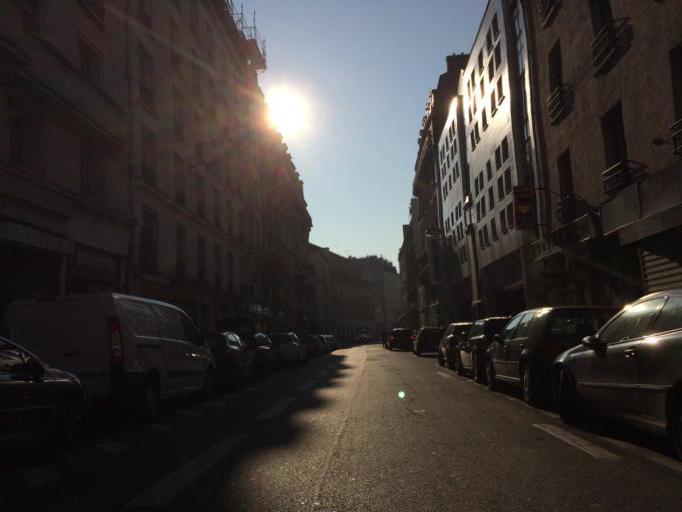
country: FR
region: Ile-de-France
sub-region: Paris
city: Paris
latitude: 48.8790
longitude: 2.3632
